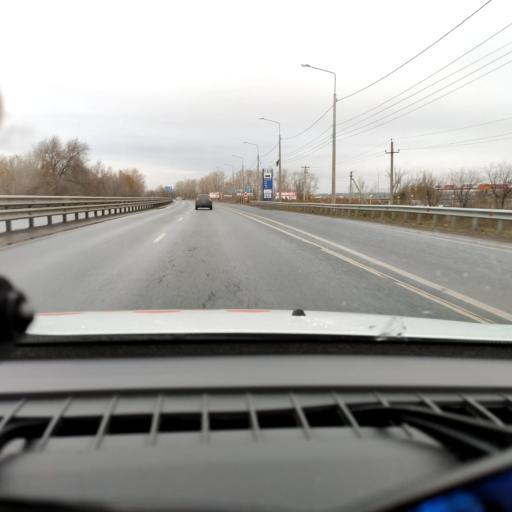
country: RU
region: Samara
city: Samara
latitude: 53.0996
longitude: 50.1602
